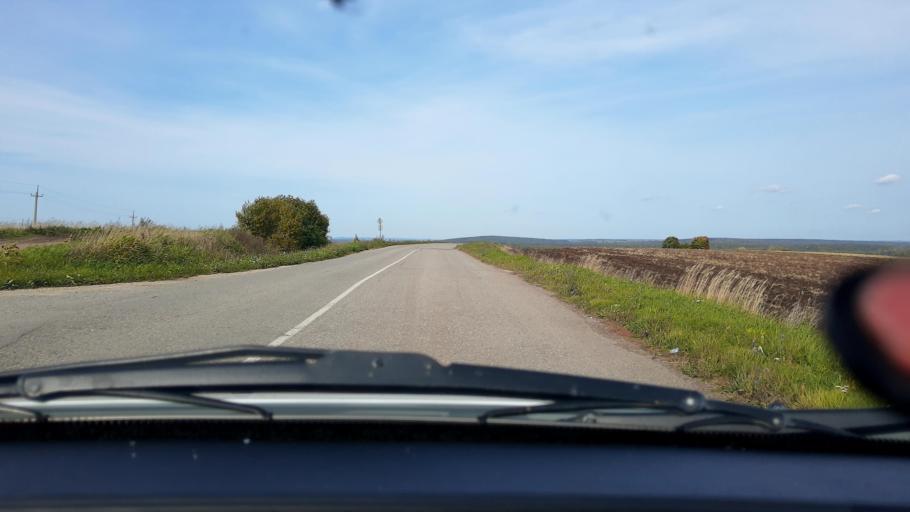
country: RU
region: Bashkortostan
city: Iglino
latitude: 54.7659
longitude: 56.5533
